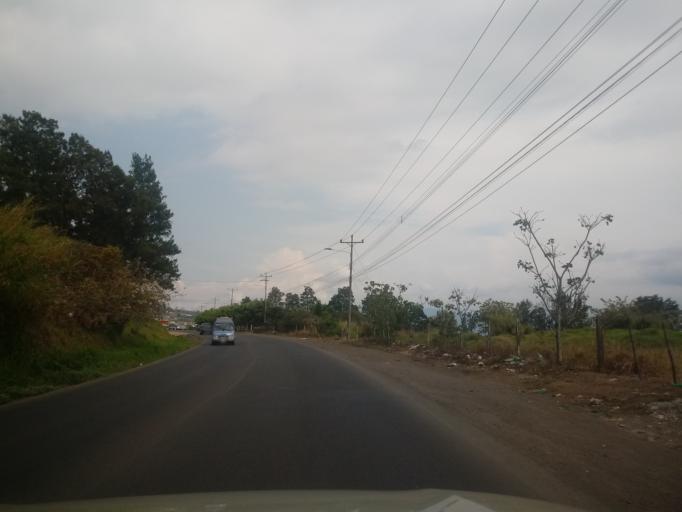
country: CR
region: Cartago
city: Cartago
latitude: 9.8792
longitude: -83.9161
